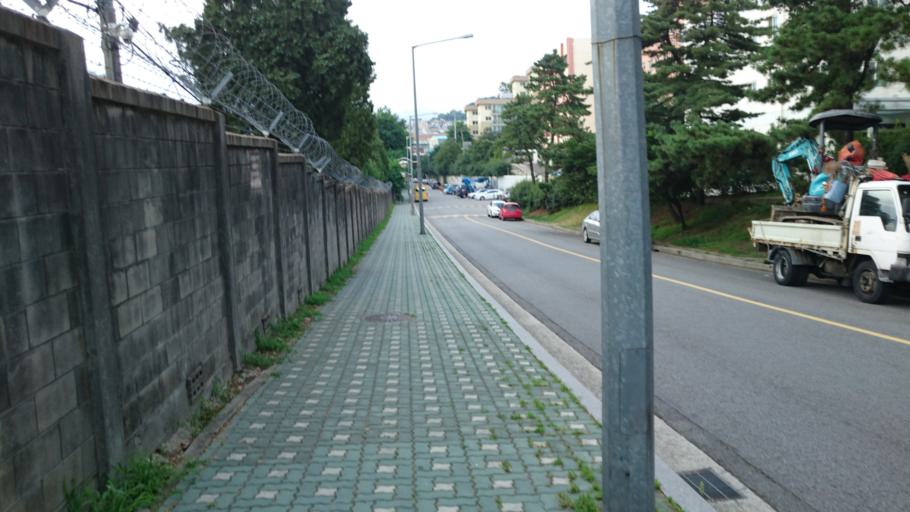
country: KR
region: Seoul
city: Seoul
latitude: 37.5421
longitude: 126.9793
